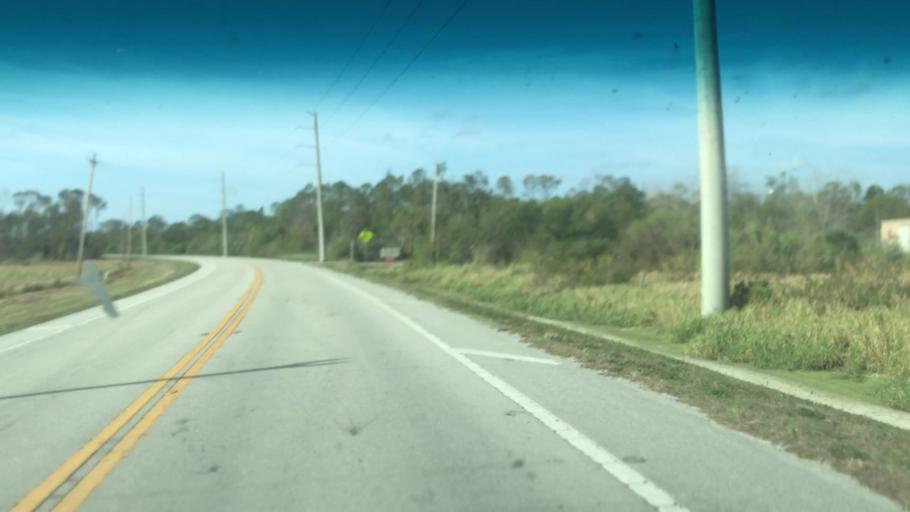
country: US
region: Florida
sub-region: Collier County
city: Orangetree
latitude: 26.3651
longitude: -81.5911
